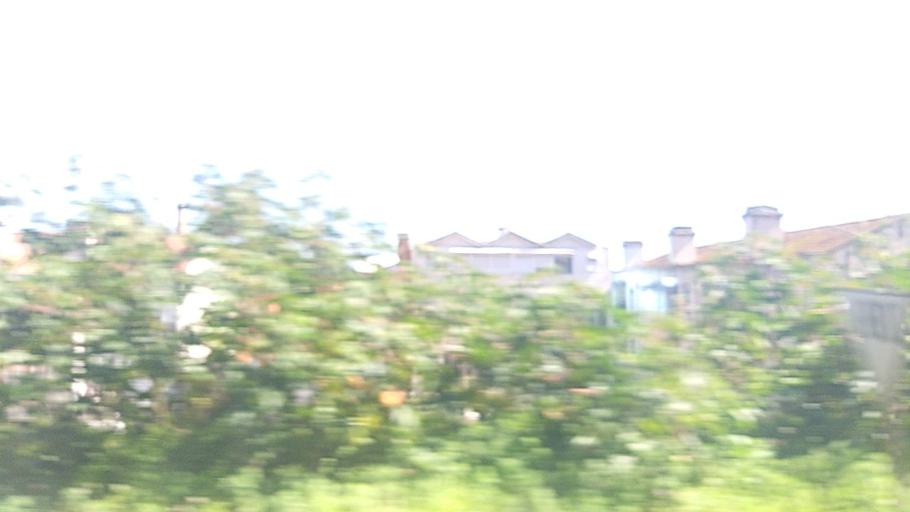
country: PT
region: Lisbon
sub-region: Lisbon
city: Lisbon
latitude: 38.7383
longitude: -9.1061
